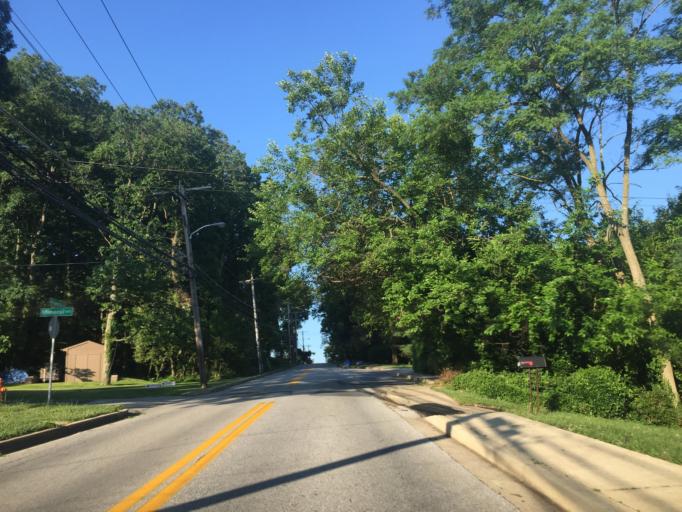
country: US
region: Maryland
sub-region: Baltimore County
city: Arbutus
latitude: 39.2365
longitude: -76.7003
